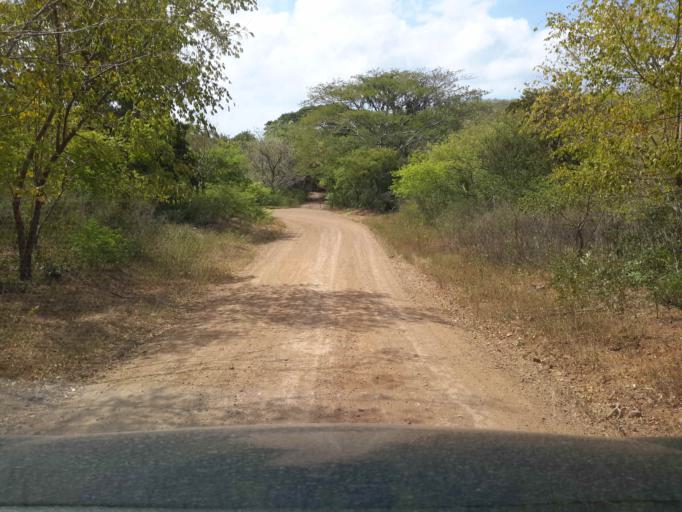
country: NI
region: Rivas
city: San Juan del Sur
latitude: 11.2112
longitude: -85.8388
